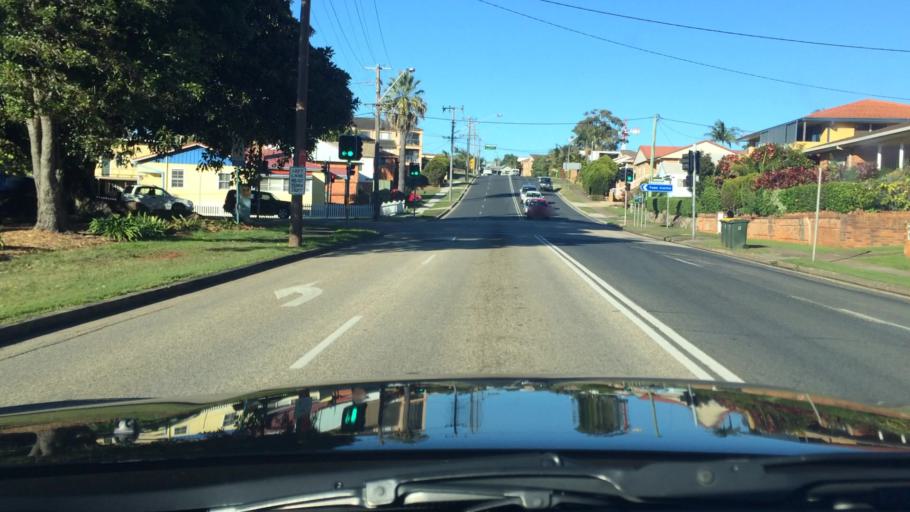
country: AU
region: New South Wales
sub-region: Port Macquarie-Hastings
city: Port Macquarie
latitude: -31.4309
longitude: 152.8997
